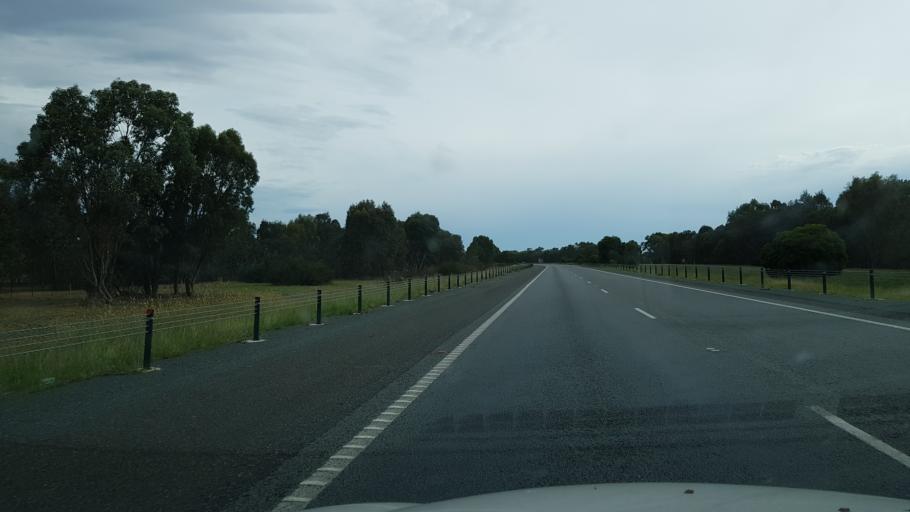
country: AU
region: Victoria
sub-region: Wangaratta
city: Wangaratta
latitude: -36.3167
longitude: 146.3740
